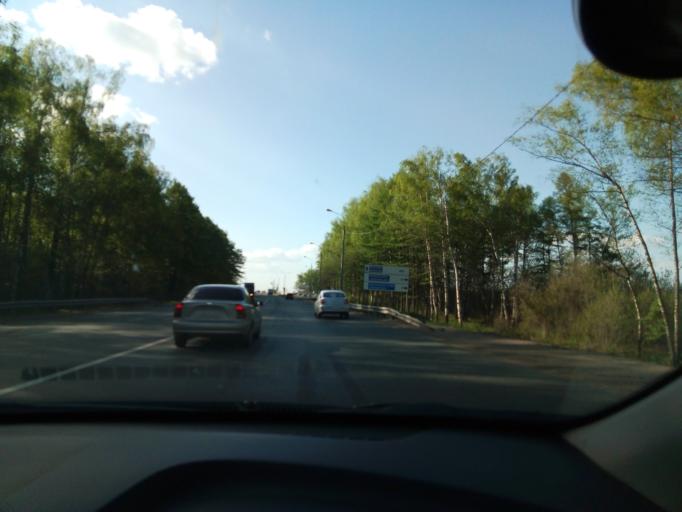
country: RU
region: Chuvashia
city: Kugesi
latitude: 56.0450
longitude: 47.2913
